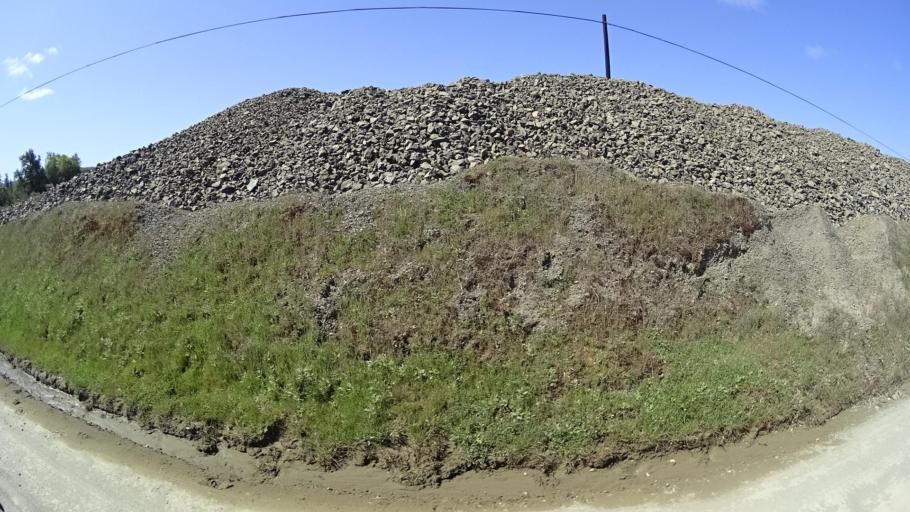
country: US
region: California
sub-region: Humboldt County
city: Redway
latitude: 40.0224
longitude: -123.6280
